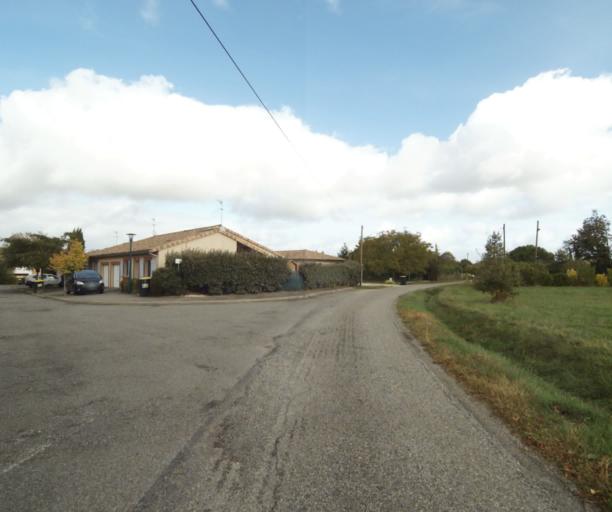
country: FR
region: Midi-Pyrenees
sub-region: Departement du Tarn-et-Garonne
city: Finhan
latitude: 43.8973
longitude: 1.1315
